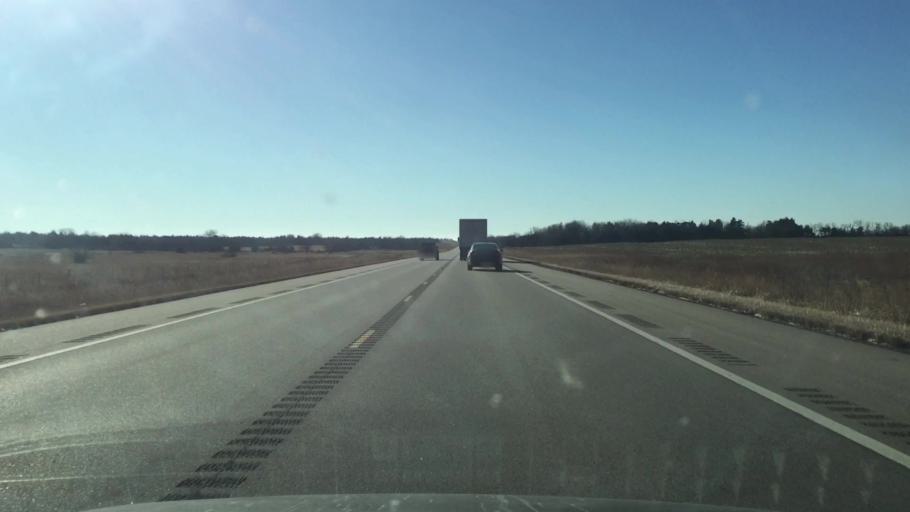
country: US
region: Kansas
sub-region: Allen County
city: Iola
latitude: 38.0434
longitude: -95.3806
